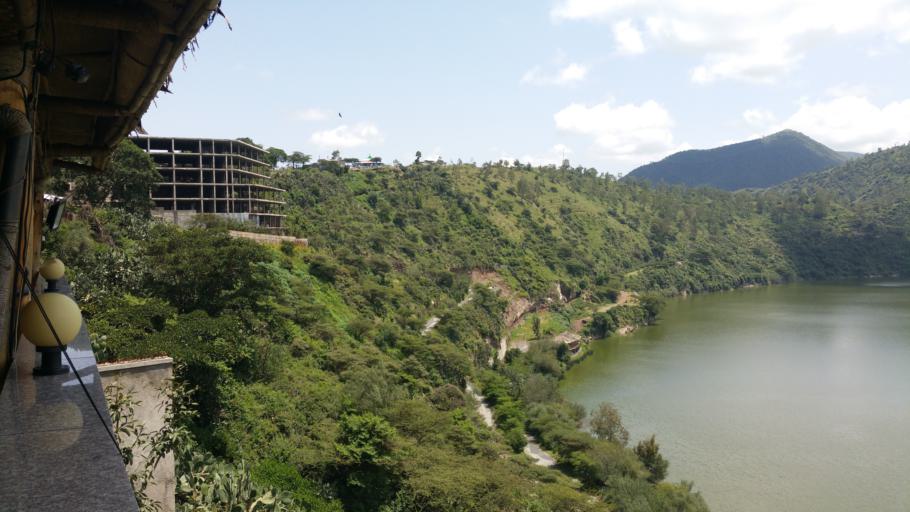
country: ET
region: Oromiya
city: Bishoftu
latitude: 8.7434
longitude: 38.9895
